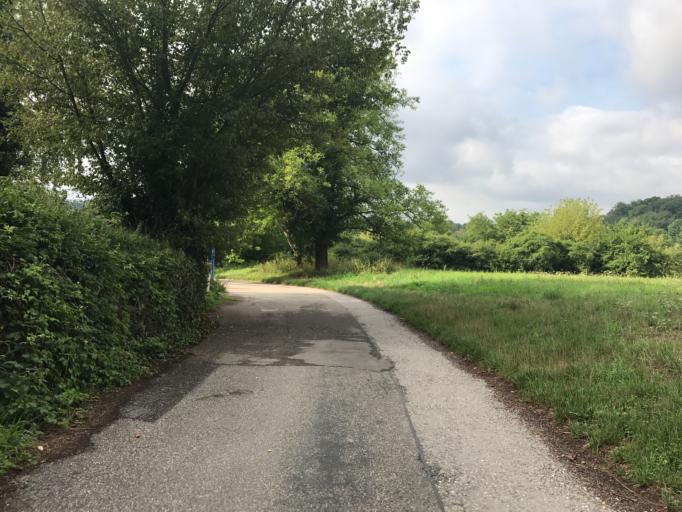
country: DE
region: Baden-Wuerttemberg
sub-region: Karlsruhe Region
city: Joehlingen
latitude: 49.0086
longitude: 8.5631
